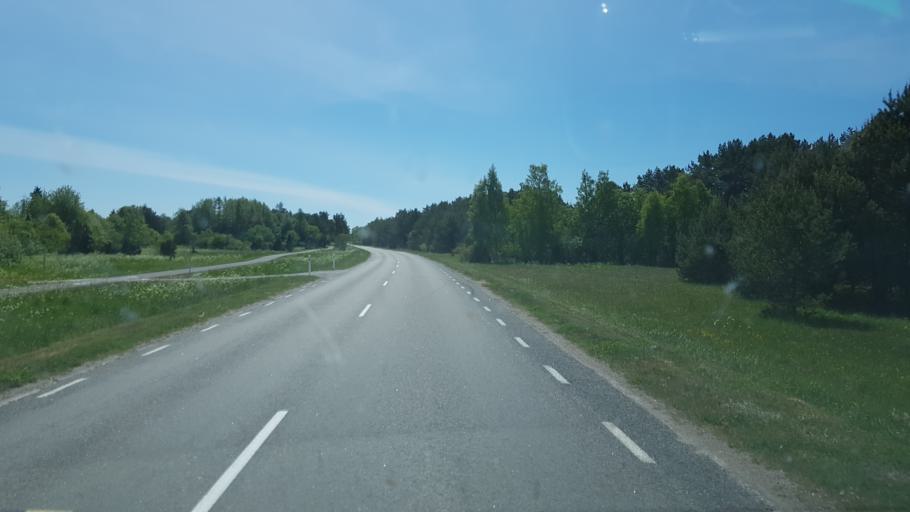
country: EE
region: Saare
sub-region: Kuressaare linn
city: Kuressaare
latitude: 58.1526
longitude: 22.2491
